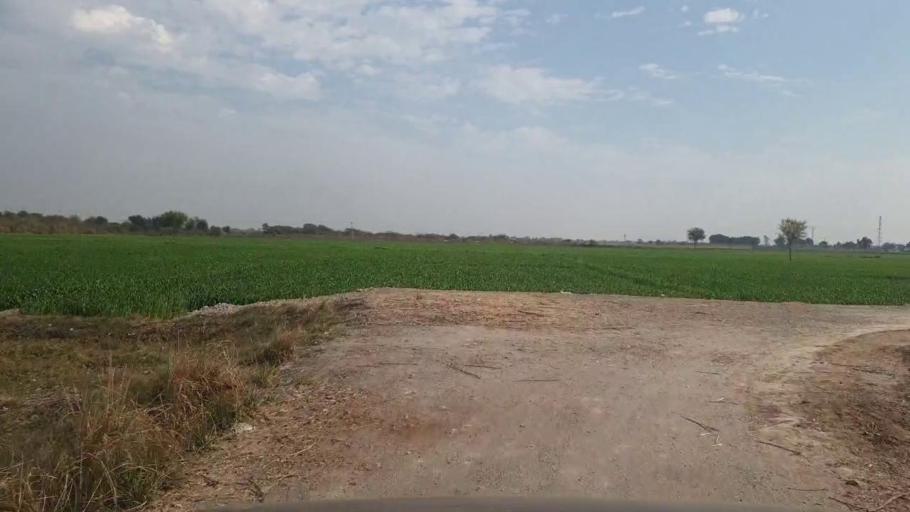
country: PK
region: Sindh
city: Sakrand
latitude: 26.0199
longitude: 68.4045
